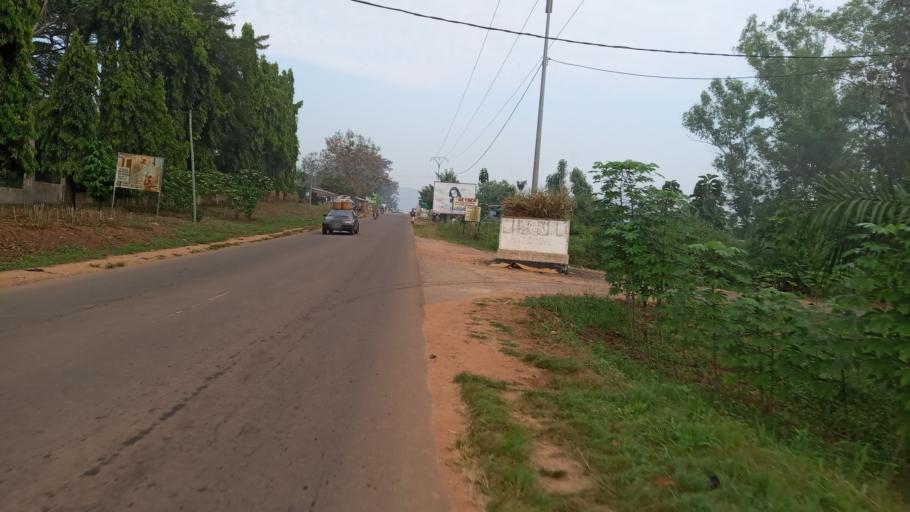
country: TG
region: Plateaux
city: Kpalime
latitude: 6.8892
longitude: 0.6426
